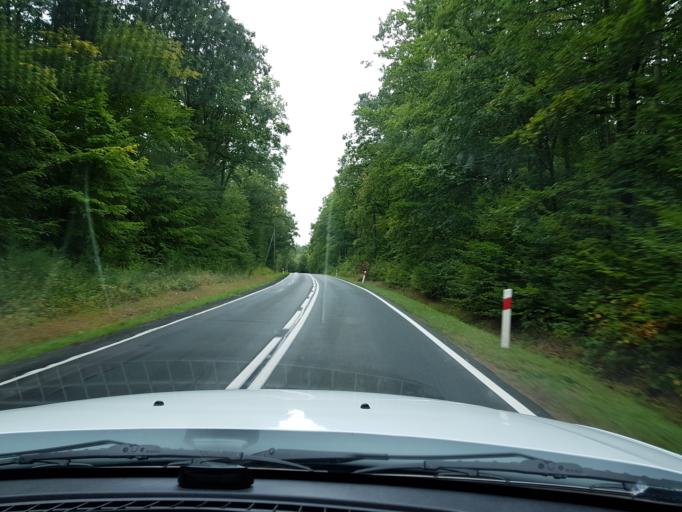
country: PL
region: West Pomeranian Voivodeship
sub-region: Powiat gryfinski
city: Widuchowa
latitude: 53.0986
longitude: 14.4186
